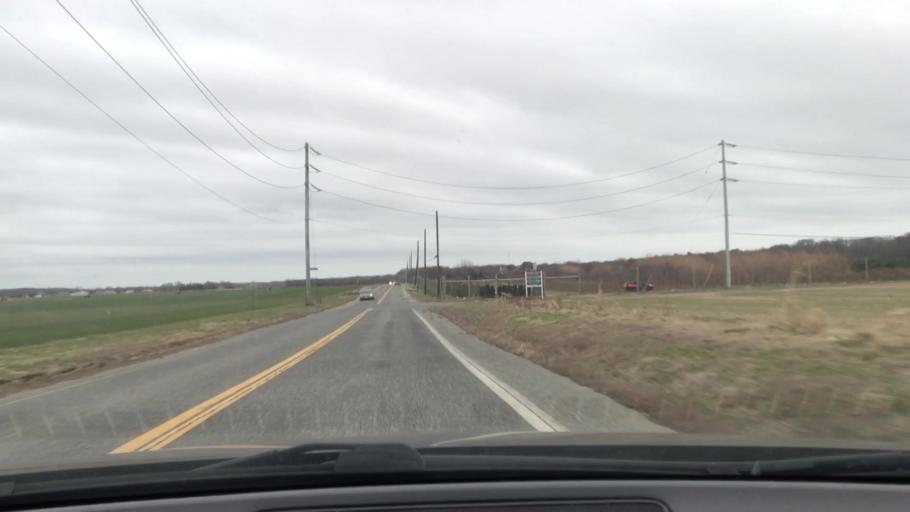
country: US
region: New York
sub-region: Suffolk County
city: Riverhead
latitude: 40.9611
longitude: -72.6700
